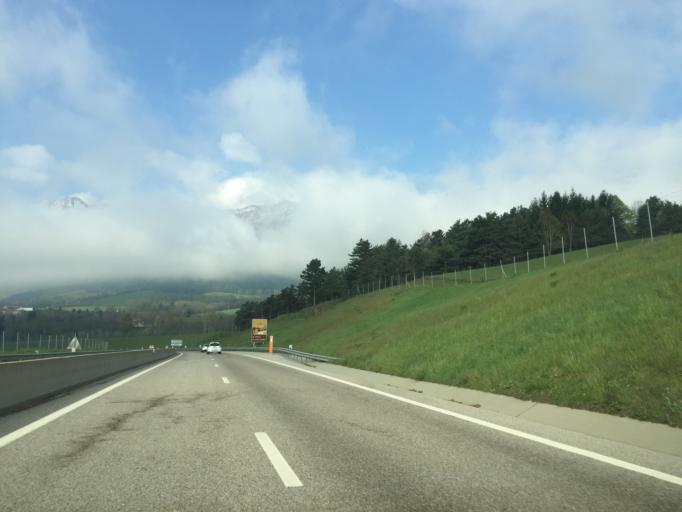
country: FR
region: Rhone-Alpes
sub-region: Departement de l'Isere
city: La Motte-Saint-Martin
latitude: 44.9181
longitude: 5.6264
